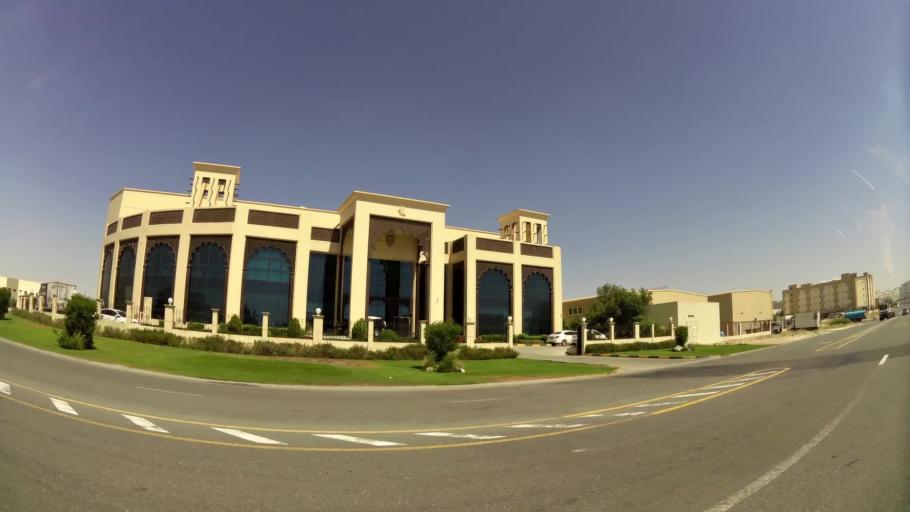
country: AE
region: Dubai
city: Dubai
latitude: 24.9710
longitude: 55.2047
